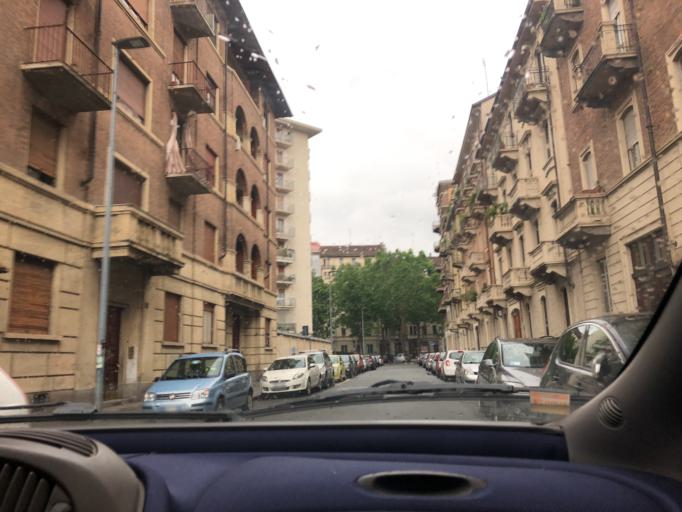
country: IT
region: Piedmont
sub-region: Provincia di Torino
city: Lesna
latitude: 45.0768
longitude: 7.6478
